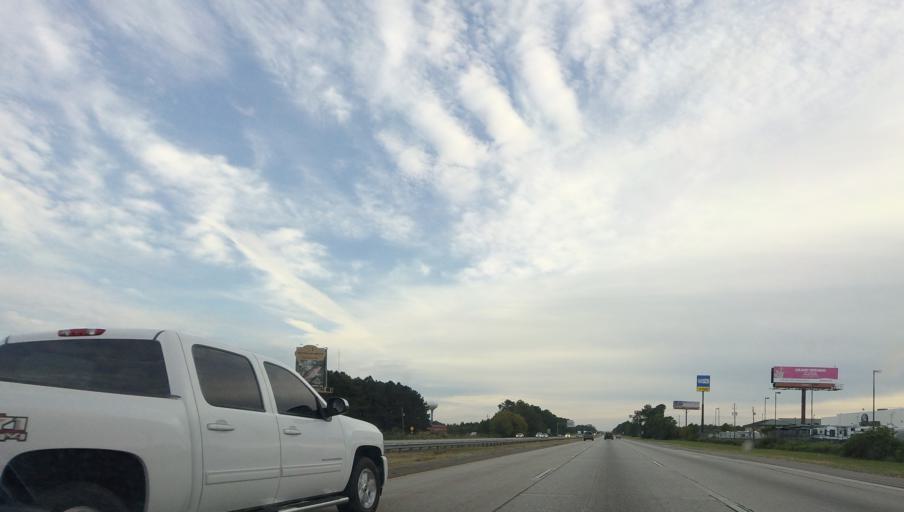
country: US
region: Georgia
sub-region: Peach County
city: Byron
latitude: 32.6537
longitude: -83.7442
